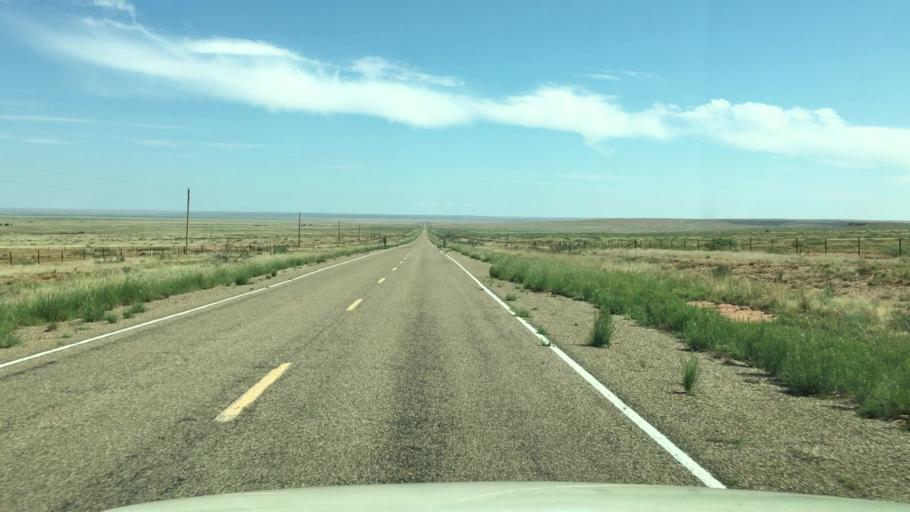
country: US
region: New Mexico
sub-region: Chaves County
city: Roswell
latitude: 33.9812
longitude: -104.5746
